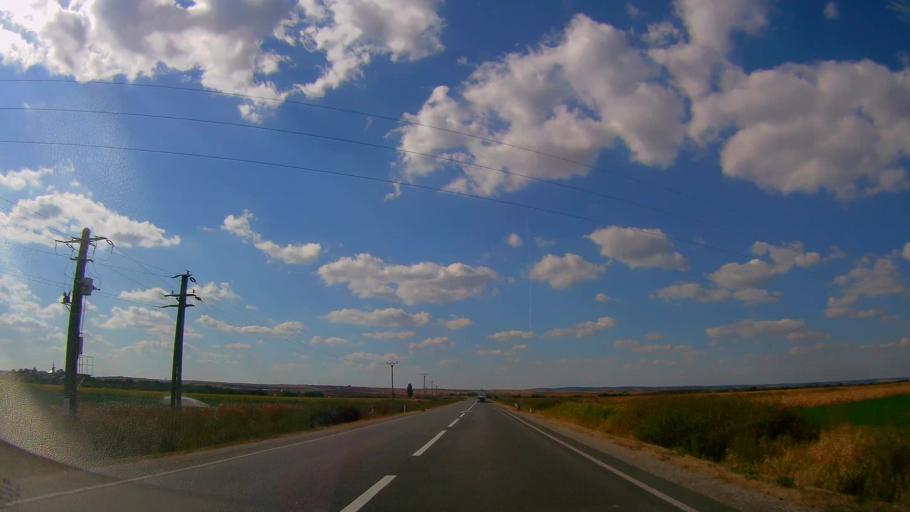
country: RO
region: Salaj
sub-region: Comuna Sarmasag
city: Sarmasag
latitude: 47.3495
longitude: 22.8118
